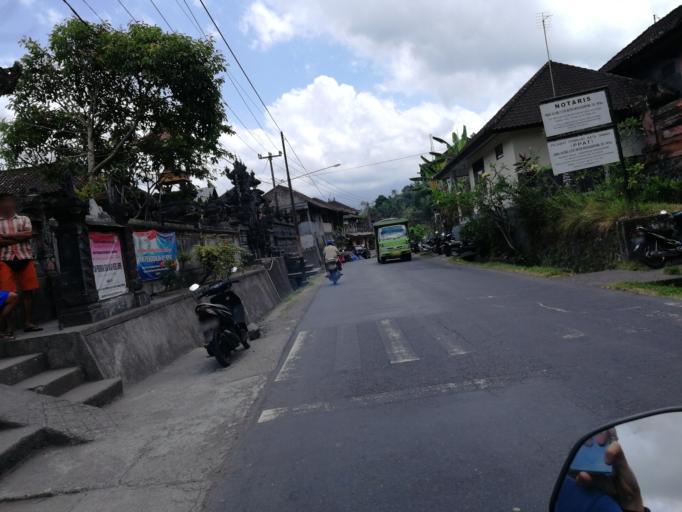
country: ID
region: Bali
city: Banjar Wangsian
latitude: -8.4637
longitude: 115.4481
